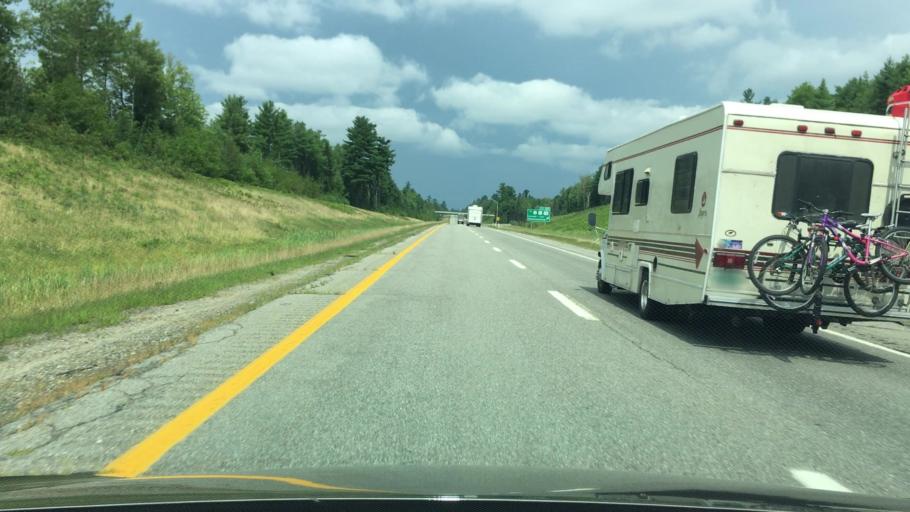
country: US
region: Maine
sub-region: Penobscot County
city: Lincoln
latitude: 45.3689
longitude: -68.6049
